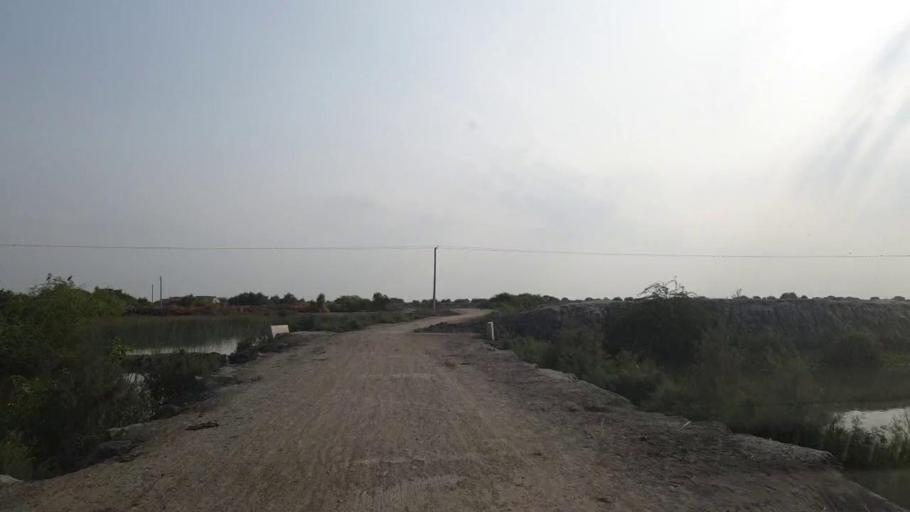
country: PK
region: Sindh
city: Kadhan
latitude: 24.4584
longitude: 68.8130
